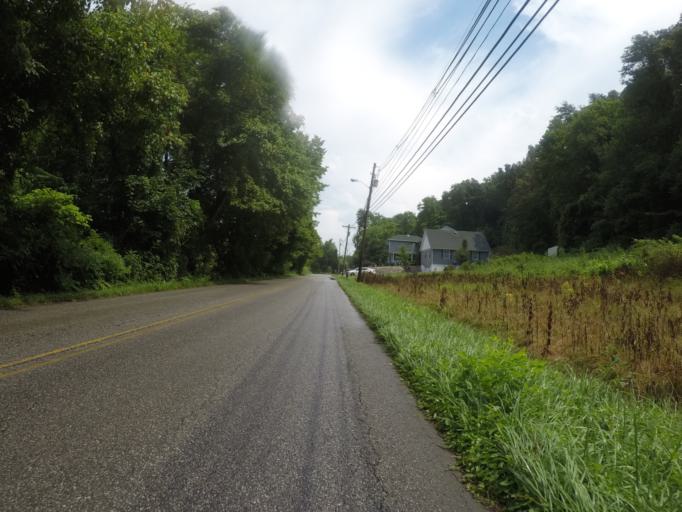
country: US
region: Kentucky
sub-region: Boyd County
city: Westwood
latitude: 38.4723
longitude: -82.6706
